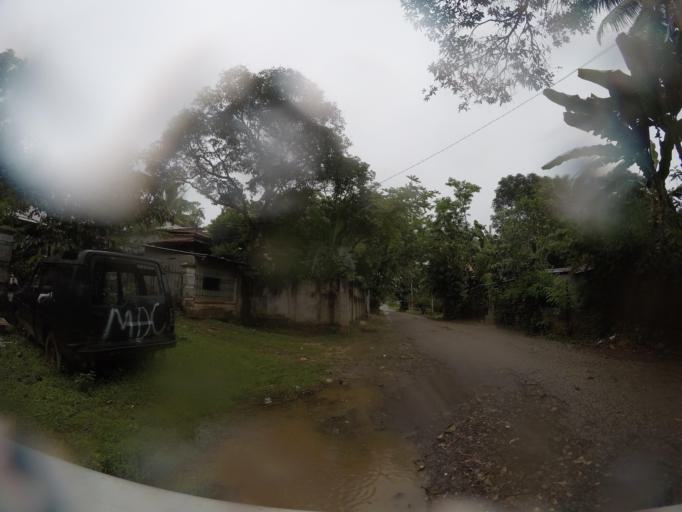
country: TL
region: Lautem
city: Lospalos
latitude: -8.5197
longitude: 127.0009
